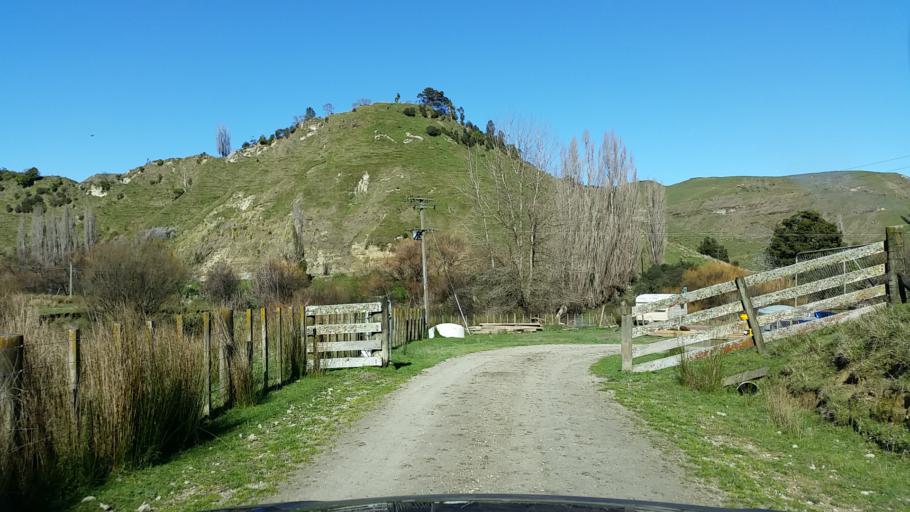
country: NZ
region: Manawatu-Wanganui
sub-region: Wanganui District
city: Wanganui
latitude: -39.6771
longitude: 174.8559
